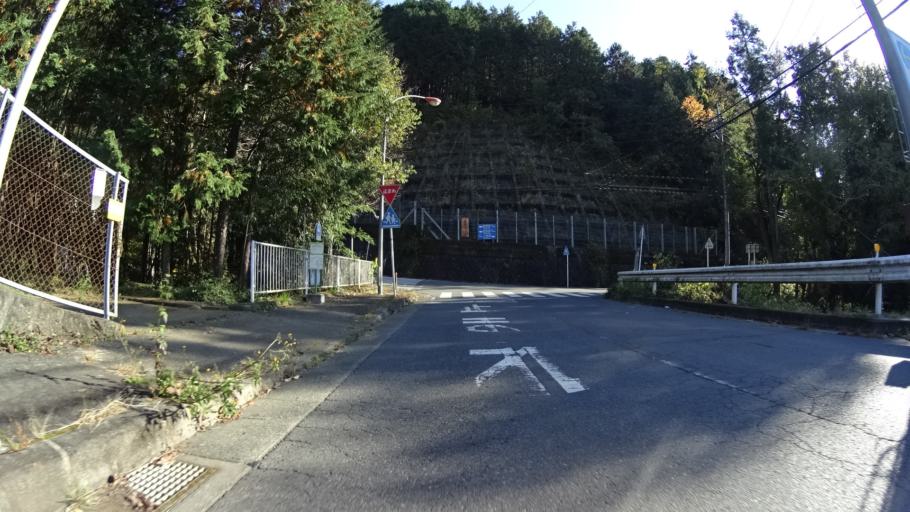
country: JP
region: Yamanashi
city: Uenohara
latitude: 35.6413
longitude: 139.1282
